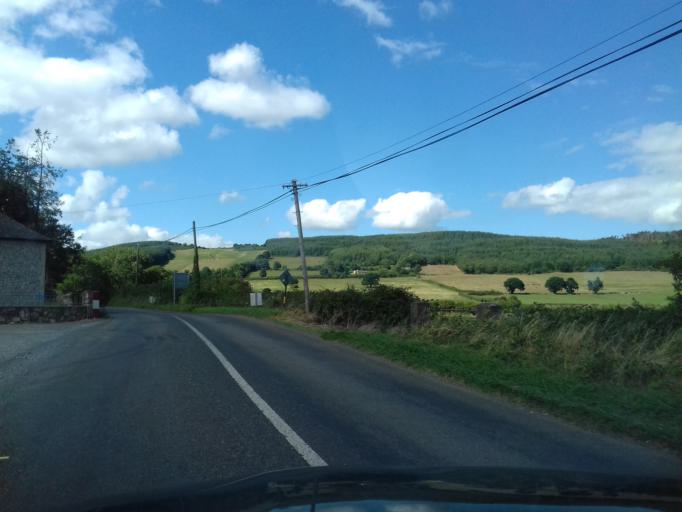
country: IE
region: Munster
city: Carrick-on-Suir
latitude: 52.3949
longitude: -7.4719
